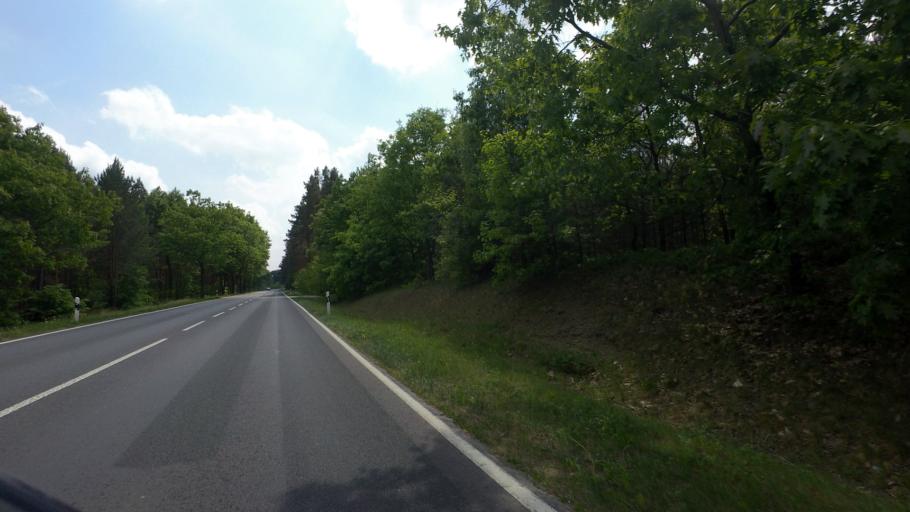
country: DE
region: Saxony
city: Niesky
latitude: 51.3191
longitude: 14.8262
